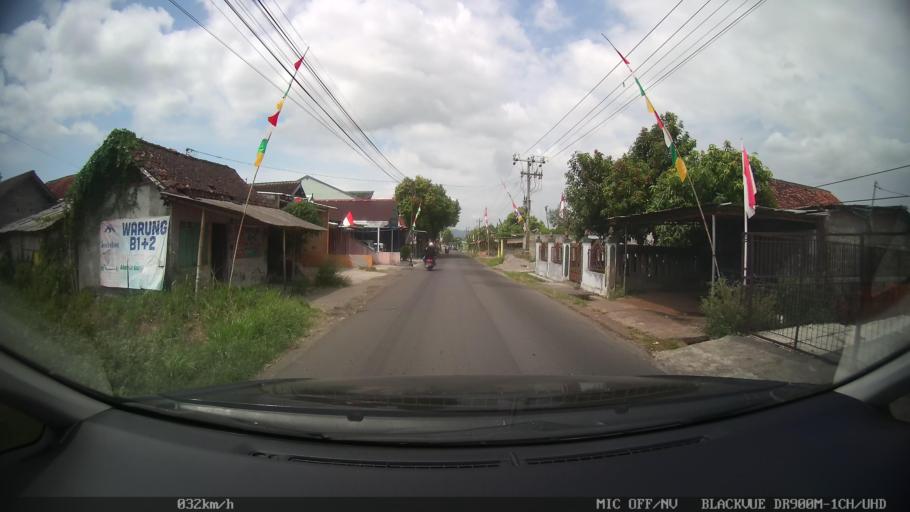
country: ID
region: Daerah Istimewa Yogyakarta
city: Depok
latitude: -7.7766
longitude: 110.4642
